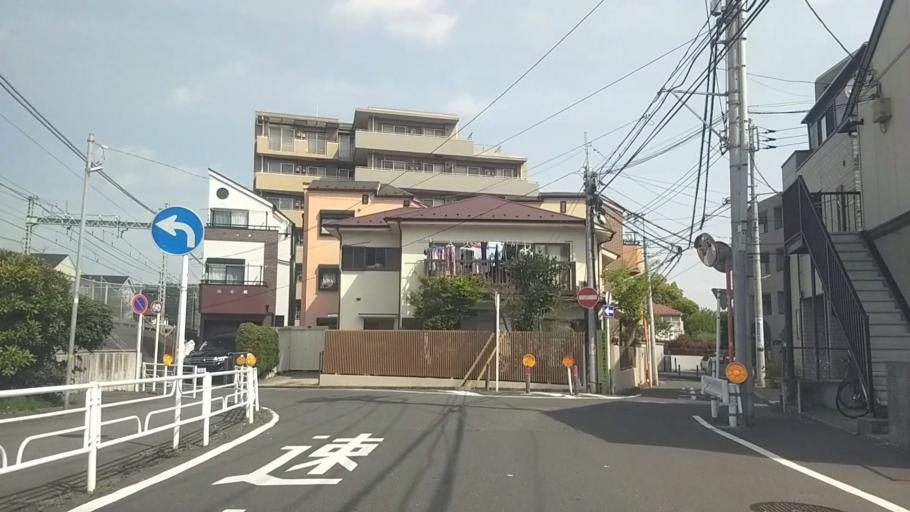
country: JP
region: Kanagawa
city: Yokohama
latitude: 35.3805
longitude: 139.6177
